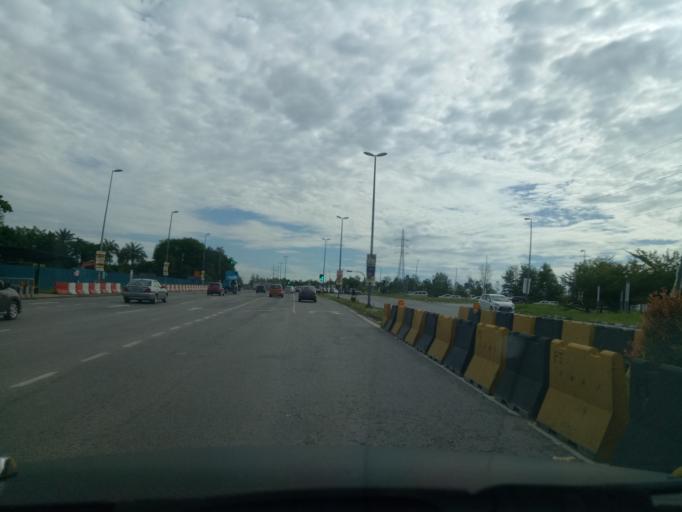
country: MY
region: Sarawak
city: Kuching
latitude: 1.4817
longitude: 110.3311
